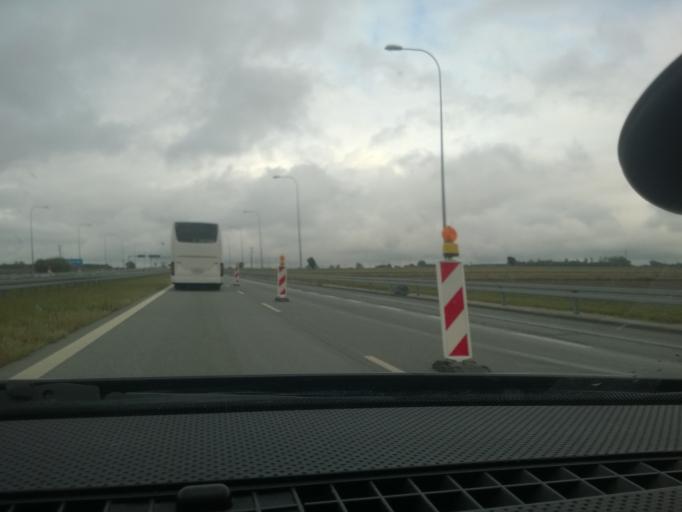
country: PL
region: Lodz Voivodeship
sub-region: Powiat zdunskowolski
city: Zapolice
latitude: 51.5932
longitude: 18.8262
